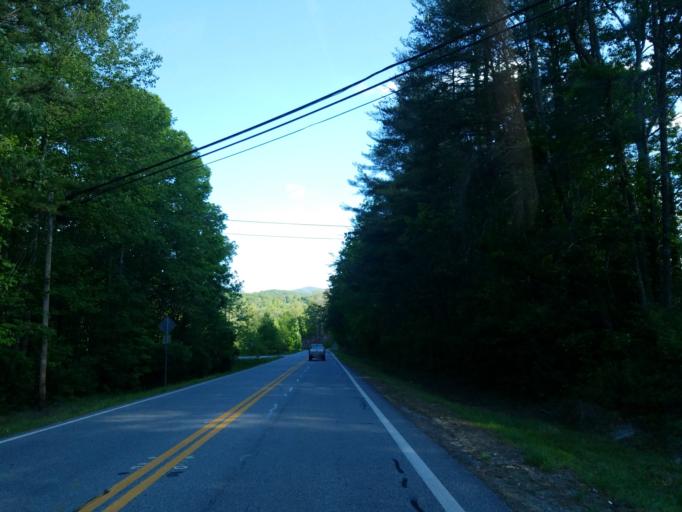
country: US
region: Georgia
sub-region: Fannin County
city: Blue Ridge
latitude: 34.8669
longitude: -84.2326
